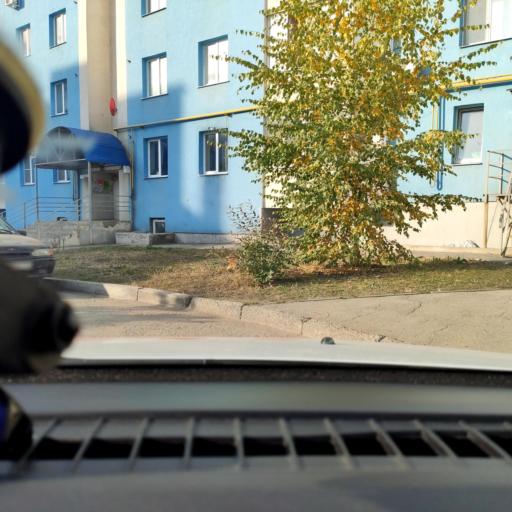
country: RU
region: Samara
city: Volzhskiy
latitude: 53.4361
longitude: 50.1257
